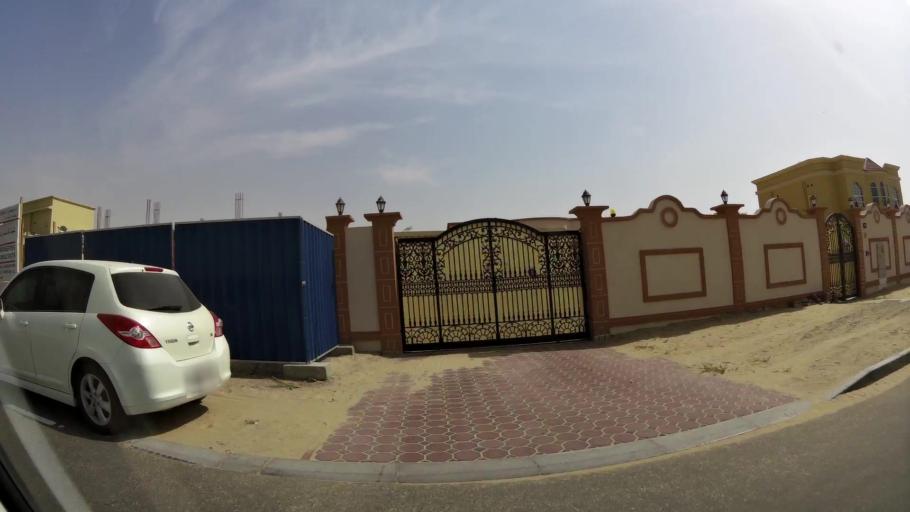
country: AE
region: Ash Shariqah
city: Sharjah
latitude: 25.2664
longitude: 55.4637
